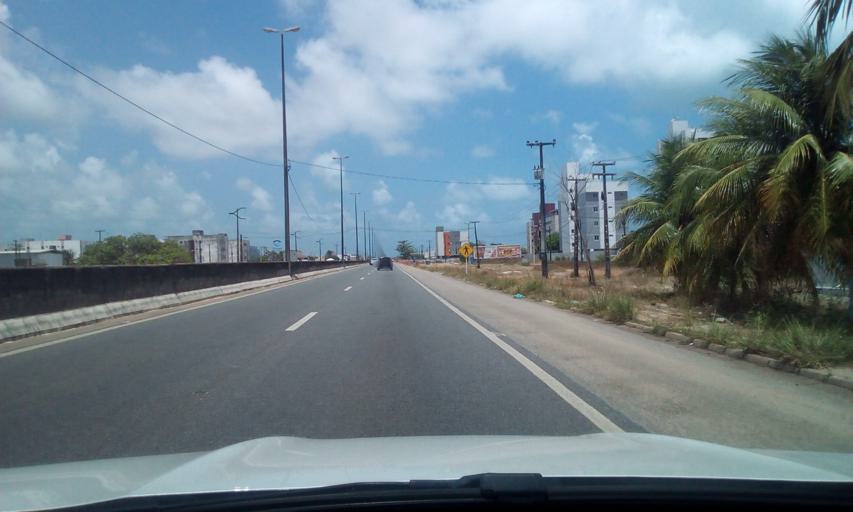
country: BR
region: Paraiba
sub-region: Cabedelo
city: Cabedelo
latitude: -7.0382
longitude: -34.8440
